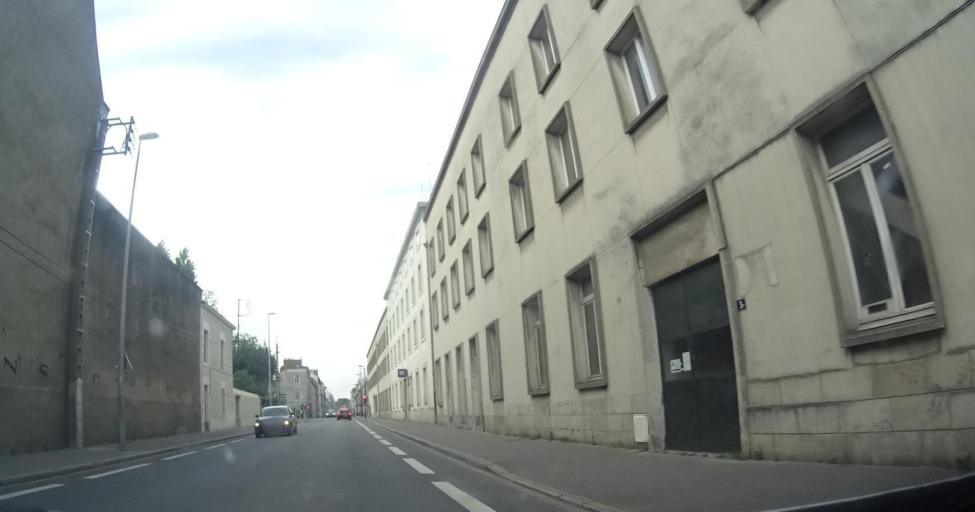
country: FR
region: Pays de la Loire
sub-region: Departement de la Loire-Atlantique
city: Nantes
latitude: 47.2230
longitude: -1.5458
